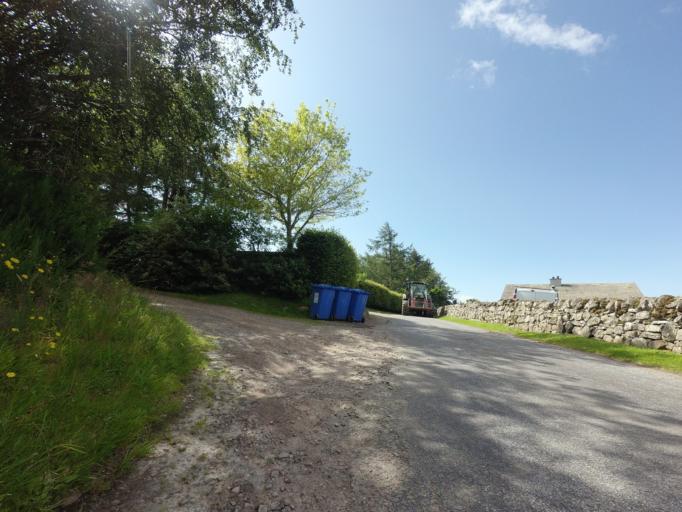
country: GB
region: Scotland
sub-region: Highland
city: Nairn
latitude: 57.5397
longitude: -3.8660
